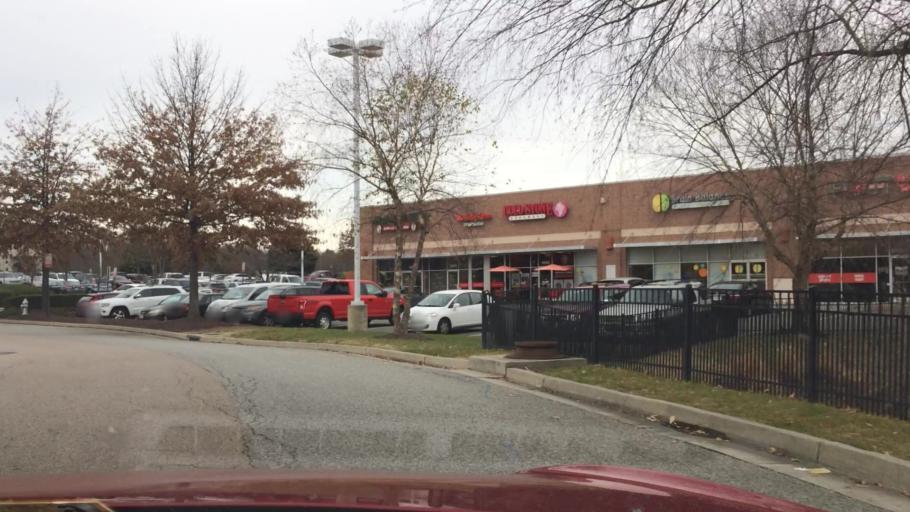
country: US
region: Virginia
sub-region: Henrico County
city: Glen Allen
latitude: 37.6706
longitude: -77.4620
